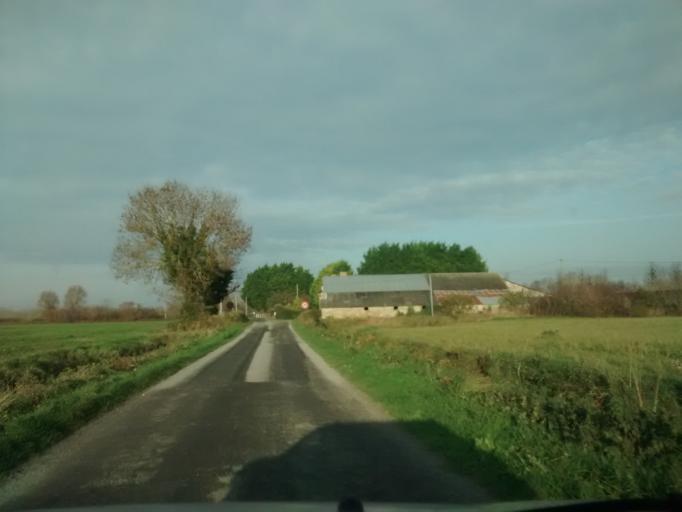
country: FR
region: Brittany
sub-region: Departement d'Ille-et-Vilaine
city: Roz-sur-Couesnon
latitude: 48.6045
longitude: -1.6016
